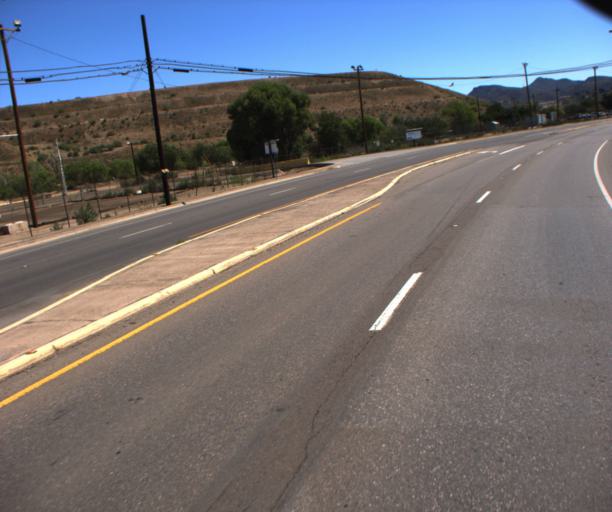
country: US
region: Arizona
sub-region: Gila County
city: Claypool
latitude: 33.4103
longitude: -110.8490
